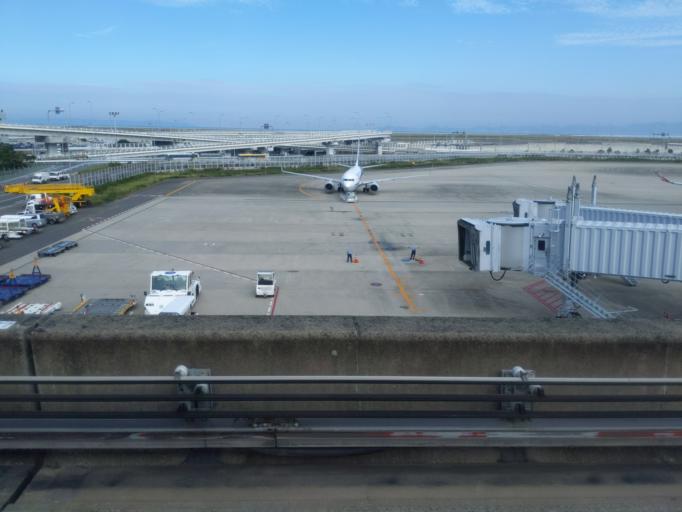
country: JP
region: Osaka
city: Kaizuka
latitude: 34.4369
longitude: 135.2486
